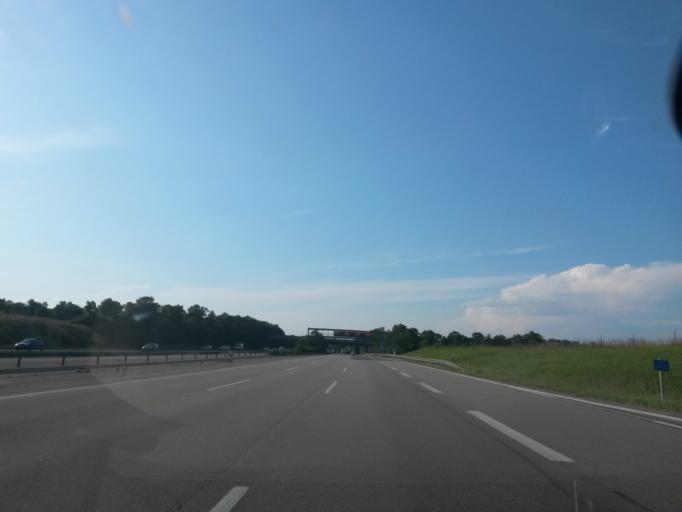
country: DE
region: Bavaria
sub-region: Upper Bavaria
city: Feldkirchen
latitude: 48.1495
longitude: 11.7552
